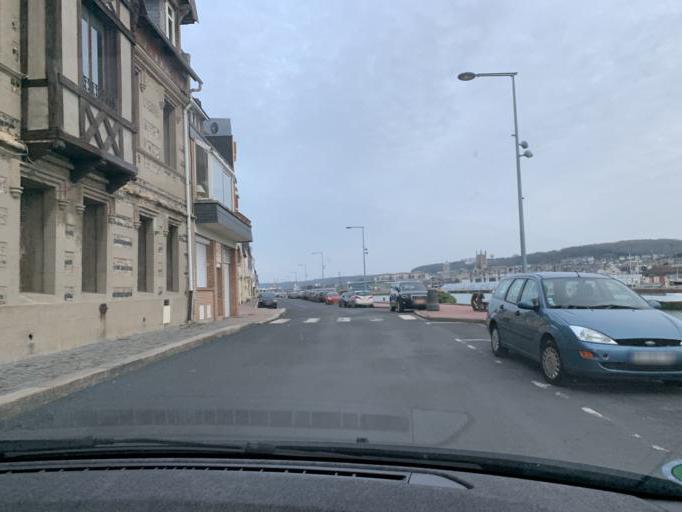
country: FR
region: Haute-Normandie
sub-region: Departement de la Seine-Maritime
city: Fecamp
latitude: 49.7638
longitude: 0.3687
